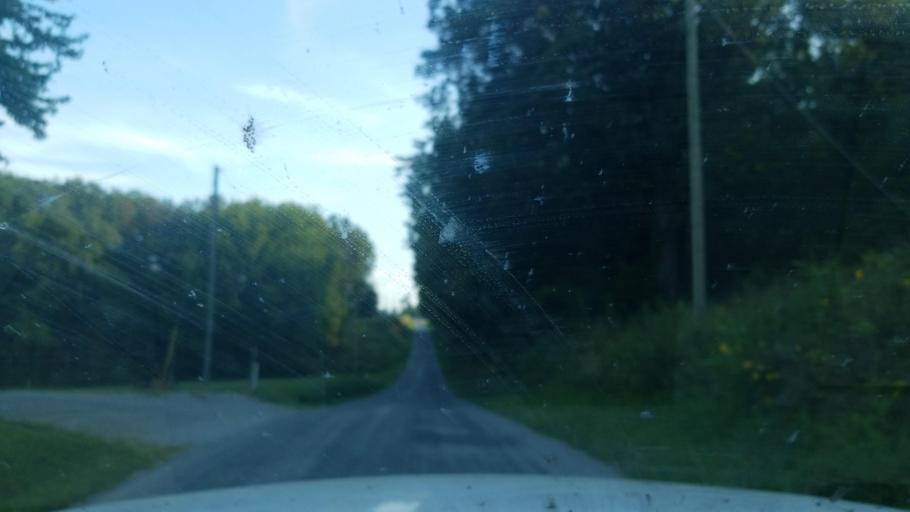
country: US
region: Illinois
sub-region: Saline County
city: Harrisburg
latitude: 37.8101
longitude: -88.6156
